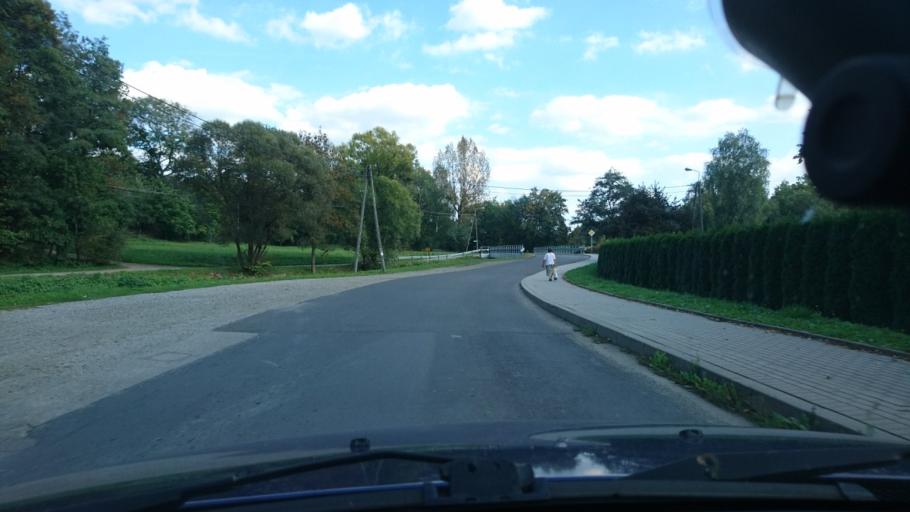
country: PL
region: Silesian Voivodeship
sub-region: Powiat bielski
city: Mazancowice
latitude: 49.8580
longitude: 18.9803
